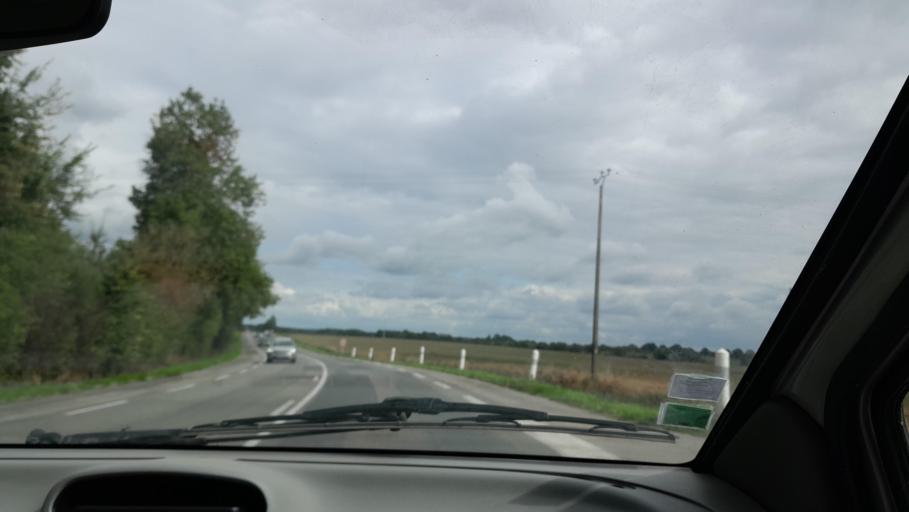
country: FR
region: Pays de la Loire
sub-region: Departement de la Mayenne
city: Ahuille
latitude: 47.9768
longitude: -0.8683
